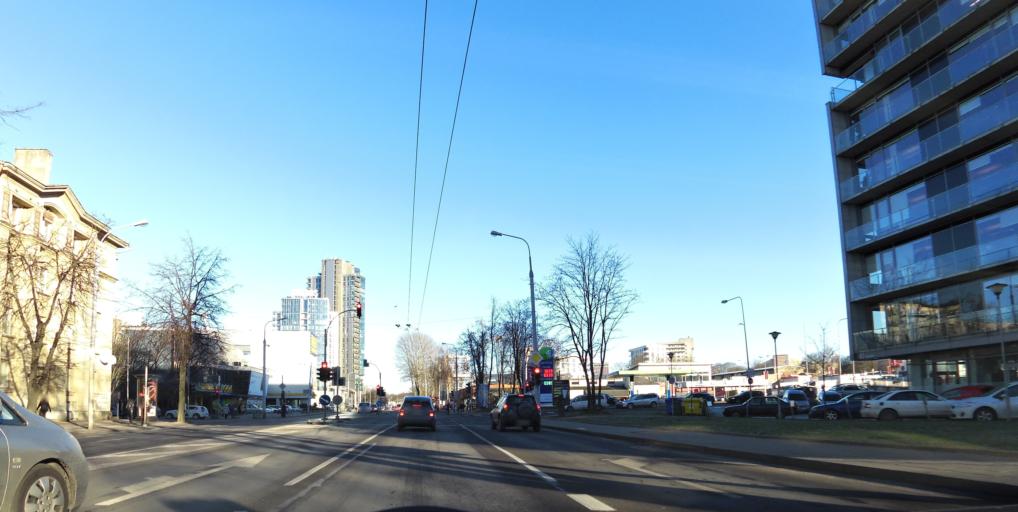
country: LT
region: Vilnius County
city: Vilkpede
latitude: 54.6770
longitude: 25.2544
